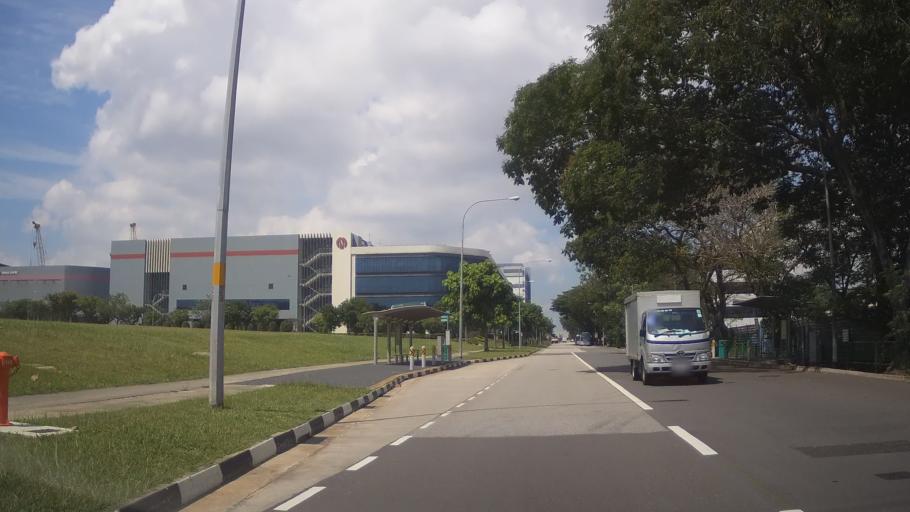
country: SG
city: Singapore
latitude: 1.3269
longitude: 103.7161
